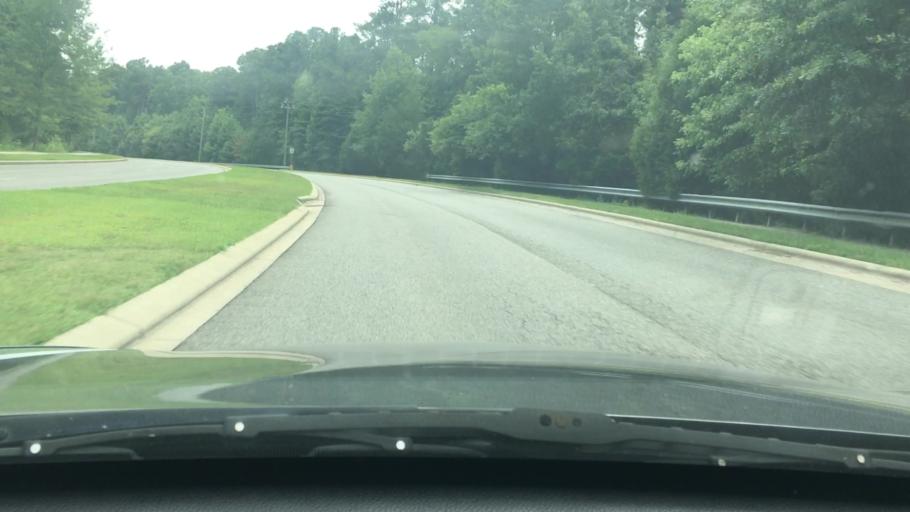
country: US
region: North Carolina
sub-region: Wake County
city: West Raleigh
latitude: 35.8423
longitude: -78.7143
